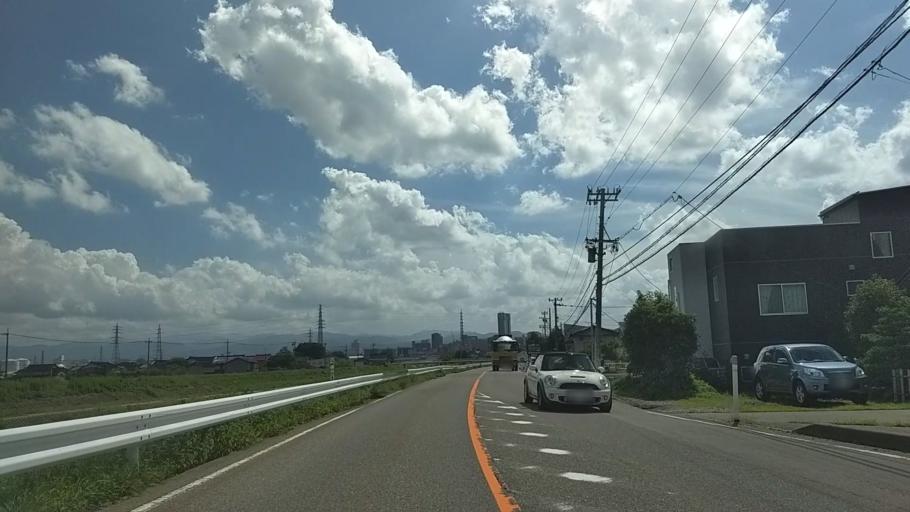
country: JP
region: Ishikawa
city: Kanazawa-shi
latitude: 36.5948
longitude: 136.6498
